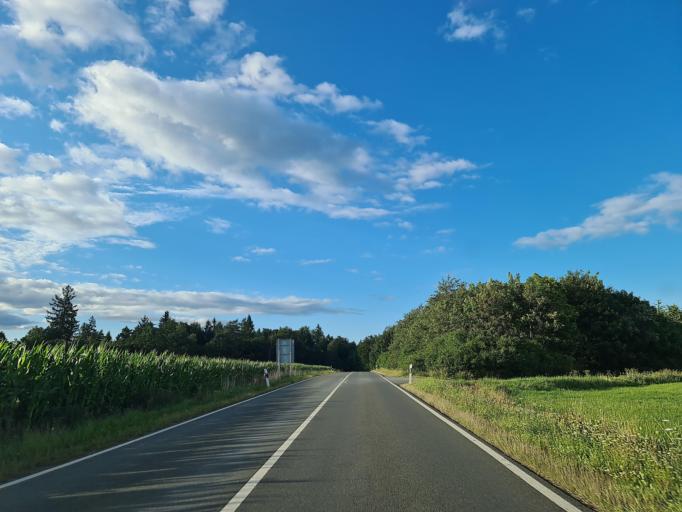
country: DE
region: Saxony
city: Pausa
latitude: 50.6008
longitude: 11.9966
